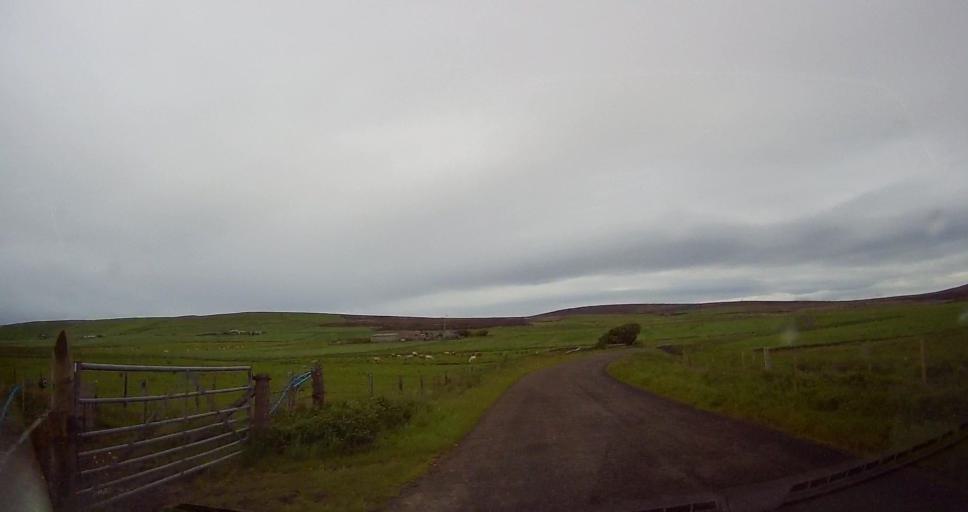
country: GB
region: Scotland
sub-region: Orkney Islands
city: Stromness
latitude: 59.0846
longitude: -3.1899
